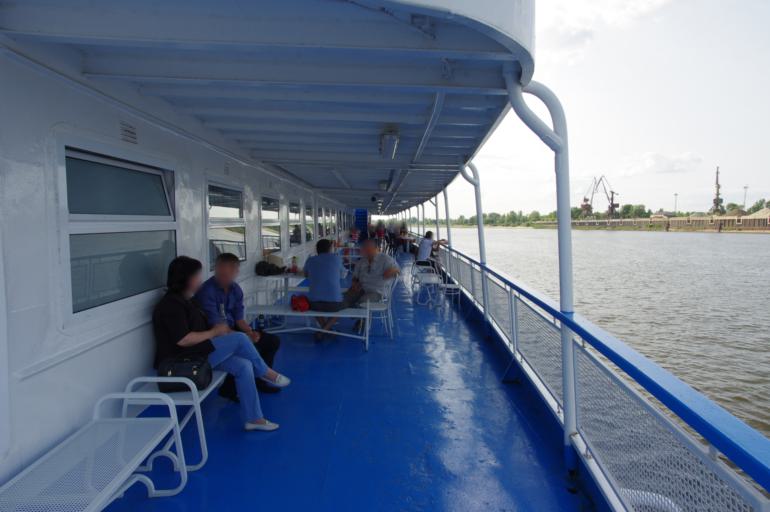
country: RU
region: Nizjnij Novgorod
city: Bor
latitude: 56.3372
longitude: 44.0773
